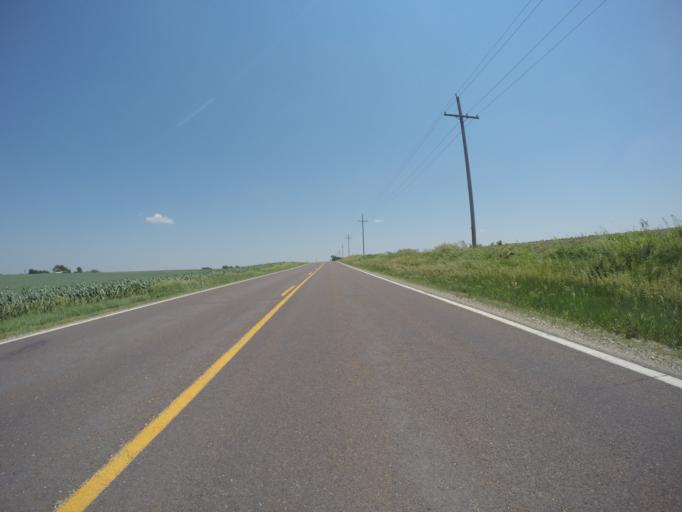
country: US
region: Kansas
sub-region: Doniphan County
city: Troy
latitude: 39.7402
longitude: -95.2039
